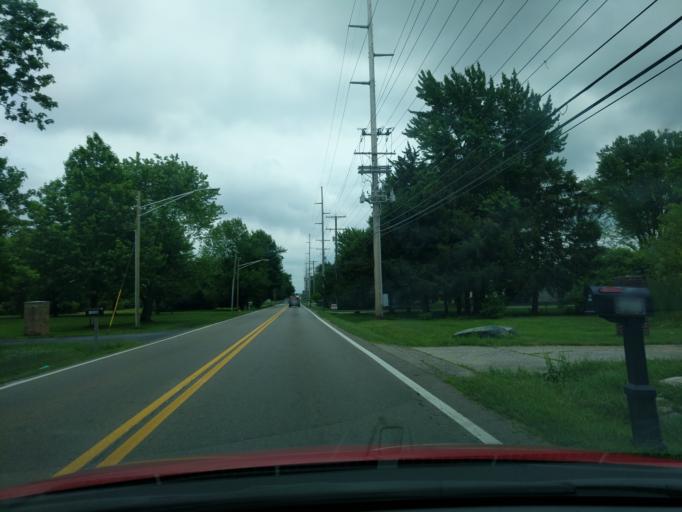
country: US
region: Ohio
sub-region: Franklin County
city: Gahanna
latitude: 40.0336
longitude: -82.9190
